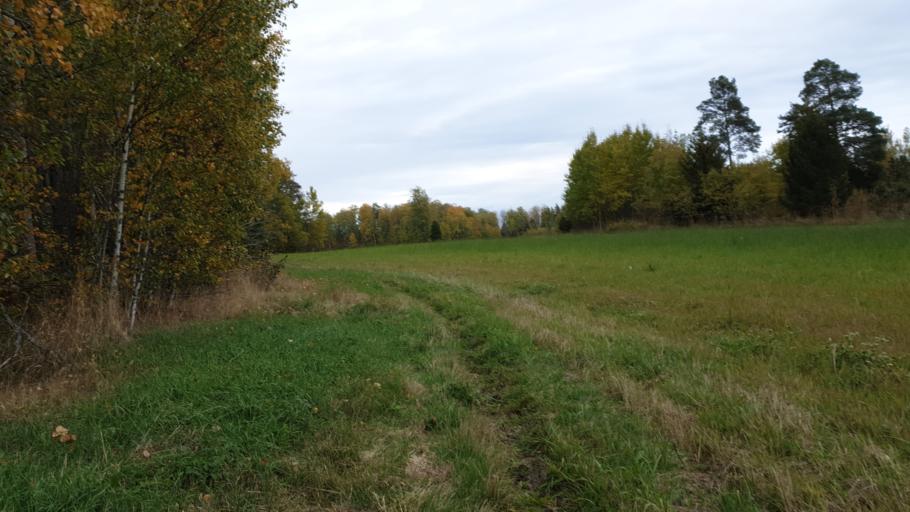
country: SE
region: Vaestmanland
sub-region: Sala Kommun
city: Sala
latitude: 59.8153
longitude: 16.6501
